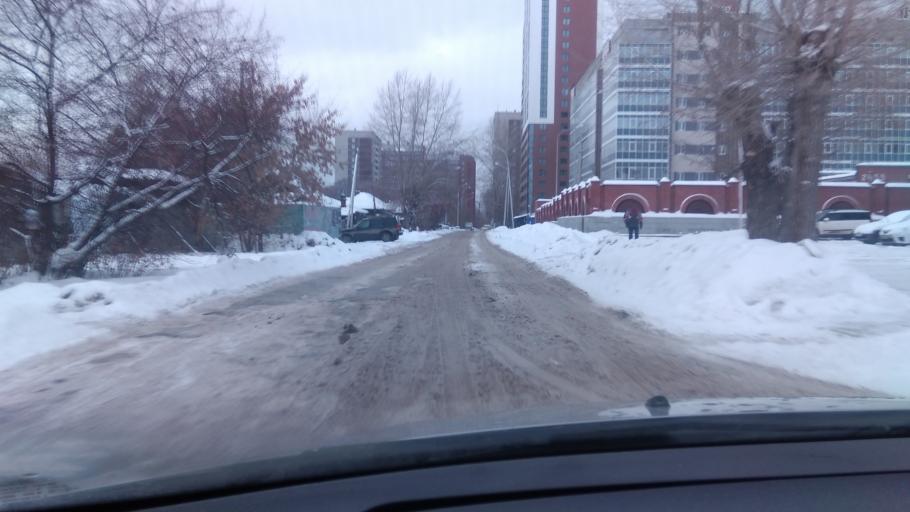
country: RU
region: Sverdlovsk
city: Yekaterinburg
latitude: 56.8042
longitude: 60.5968
